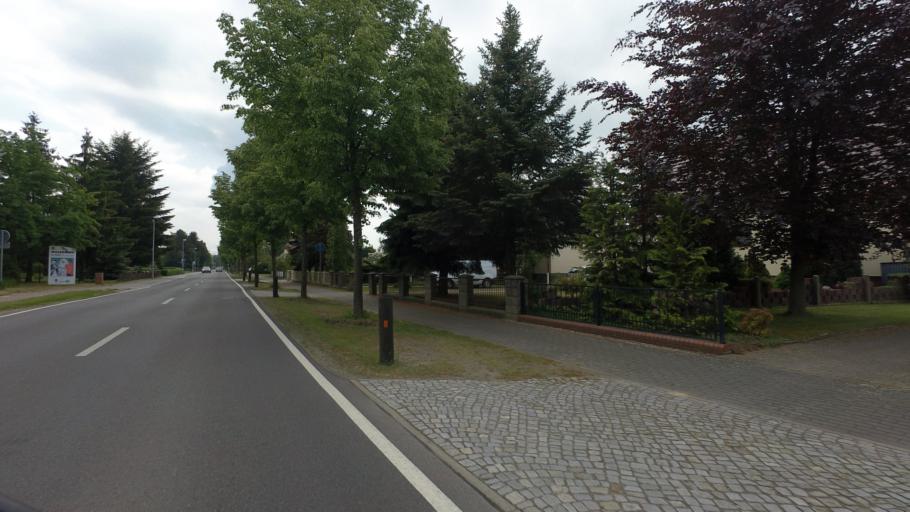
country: DE
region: Brandenburg
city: Peitz
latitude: 51.8636
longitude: 14.3951
